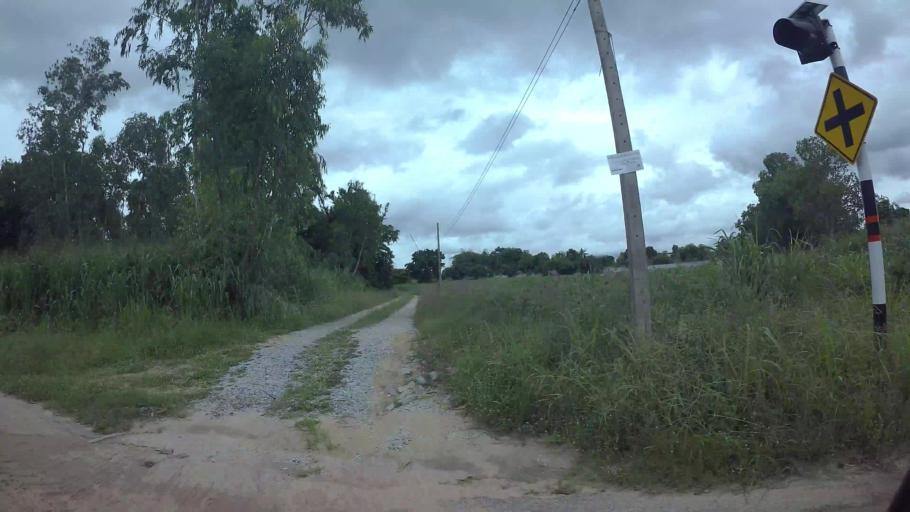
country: TH
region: Chon Buri
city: Si Racha
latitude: 13.1689
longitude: 100.9854
